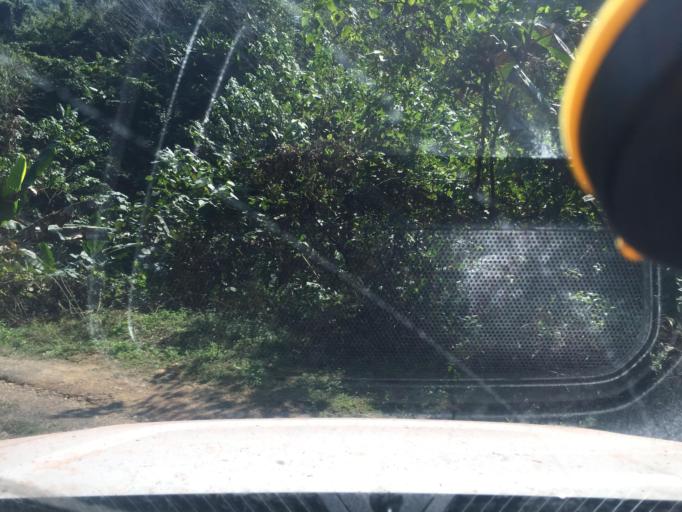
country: LA
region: Phongsali
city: Phongsali
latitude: 21.6848
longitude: 102.4069
